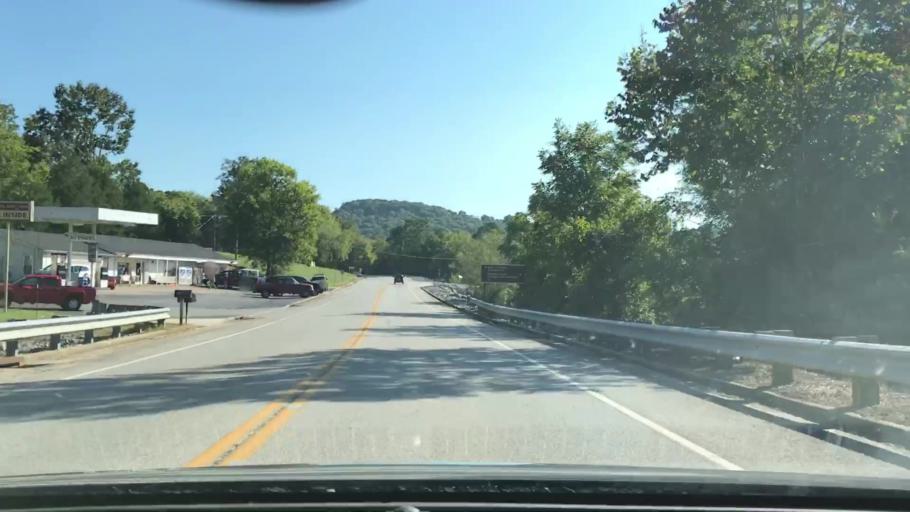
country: US
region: Tennessee
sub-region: Smith County
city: Carthage
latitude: 36.3200
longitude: -85.9104
